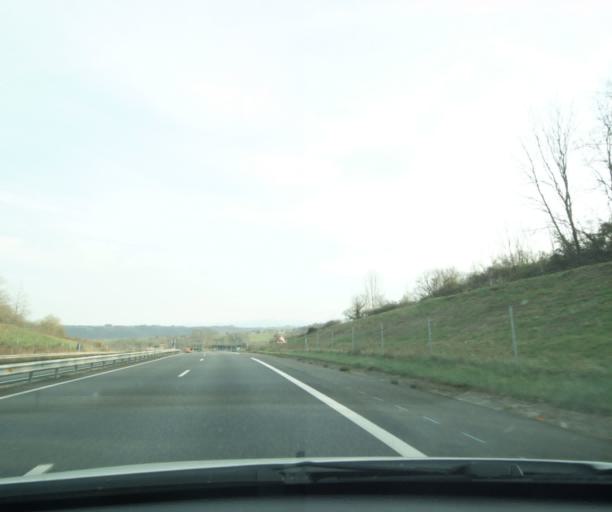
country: FR
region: Midi-Pyrenees
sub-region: Departement des Hautes-Pyrenees
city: Barbazan-Debat
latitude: 43.2015
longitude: 0.1491
